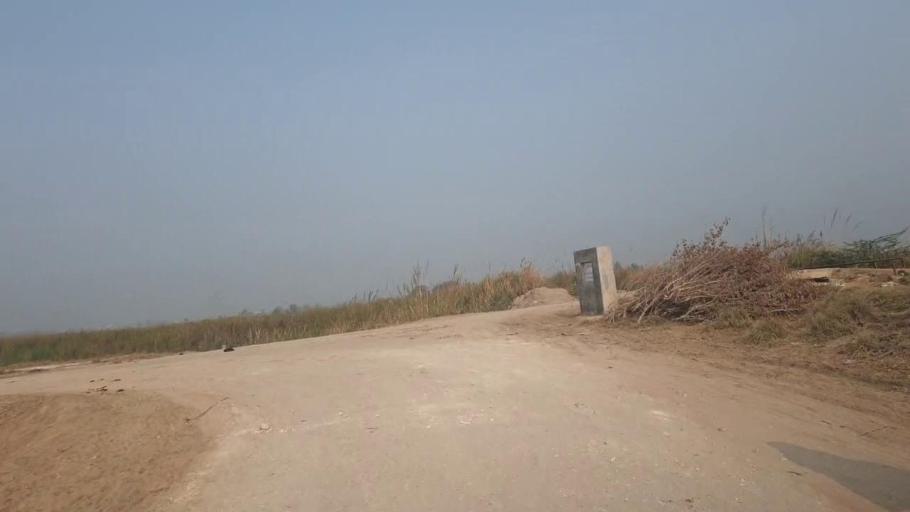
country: PK
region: Sindh
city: Shahdadpur
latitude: 25.8958
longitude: 68.5924
